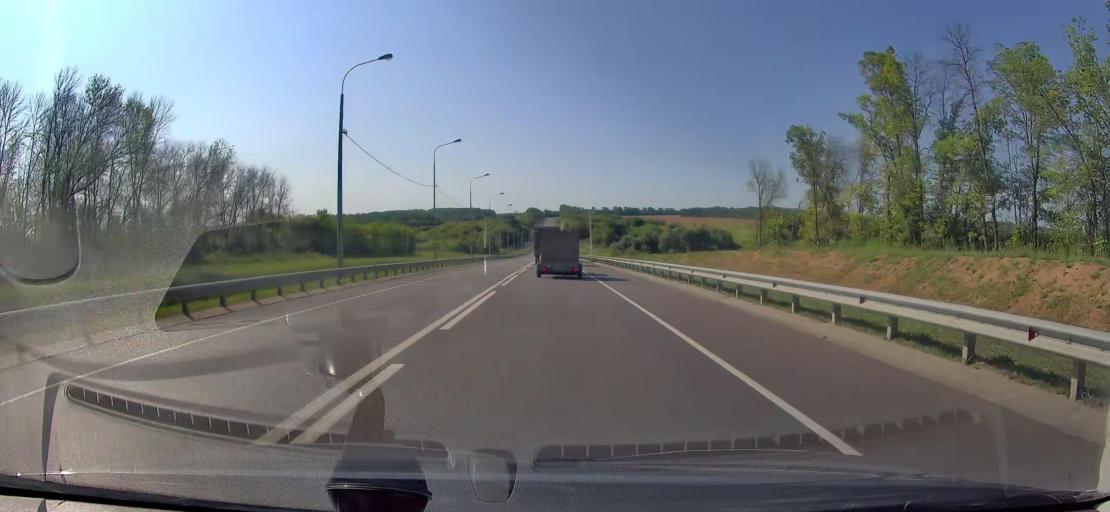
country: RU
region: Orjol
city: Kromy
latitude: 52.6244
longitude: 35.7572
